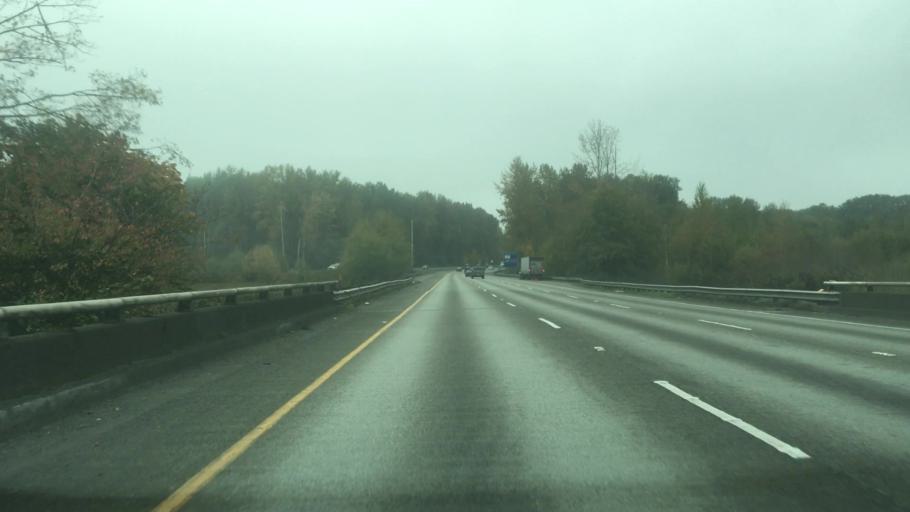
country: US
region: Washington
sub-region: Pierce County
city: DuPont
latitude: 47.0757
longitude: -122.6963
